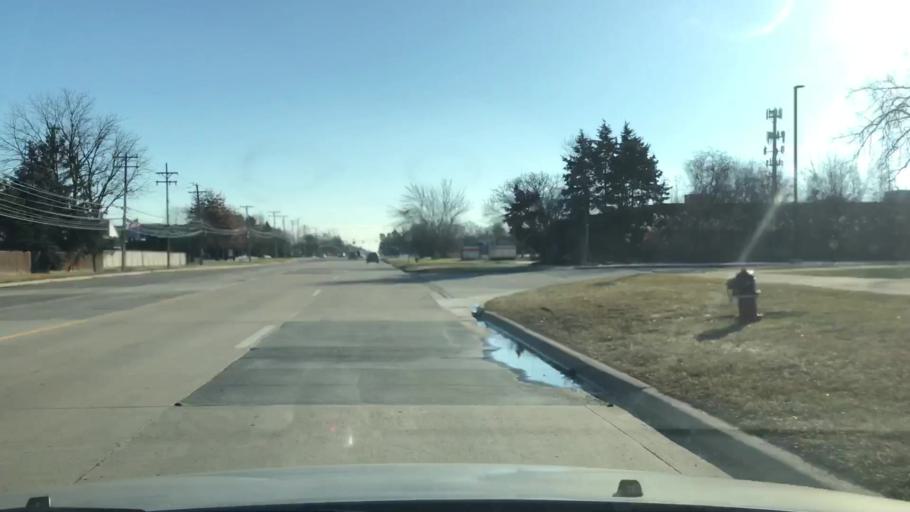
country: US
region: Michigan
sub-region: Oakland County
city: Troy
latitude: 42.5809
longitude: -83.1091
